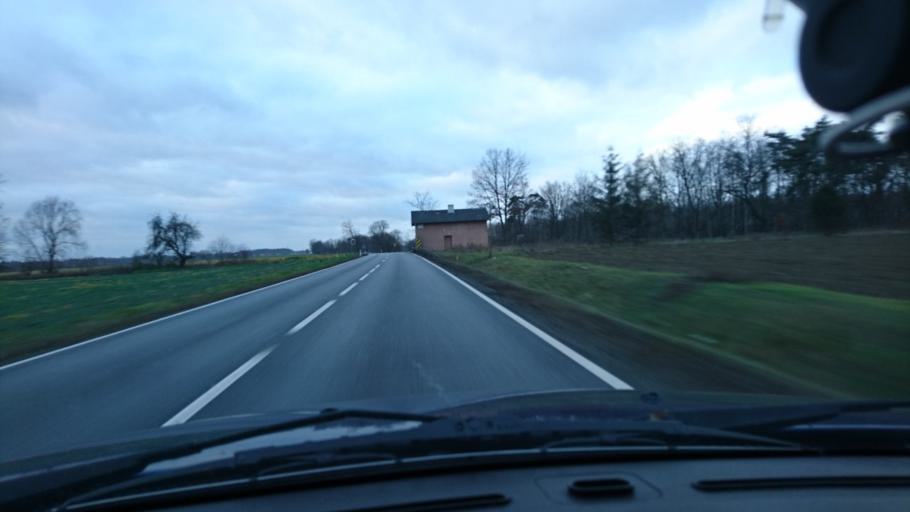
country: PL
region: Lodz Voivodeship
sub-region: Powiat wieruszowski
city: Boleslawiec
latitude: 51.1526
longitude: 18.1806
